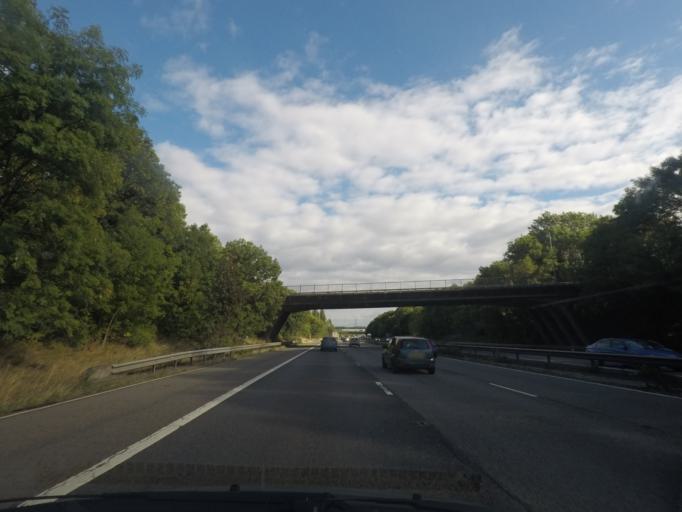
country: GB
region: England
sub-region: Leicestershire
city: Kirby Muxloe
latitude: 52.6528
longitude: -1.2392
